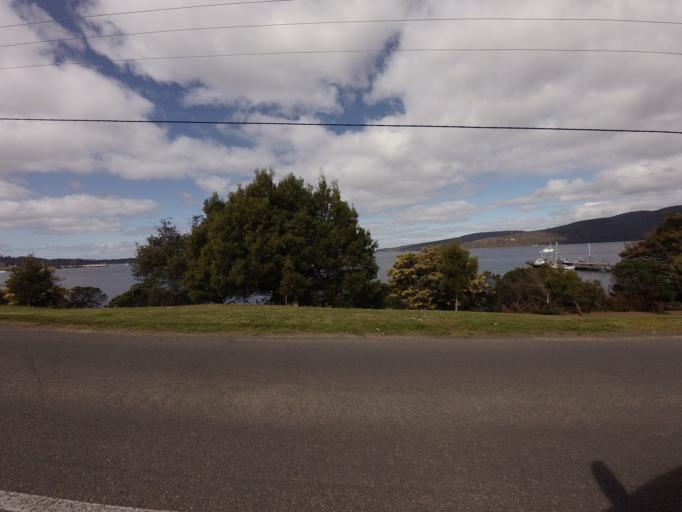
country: AU
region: Tasmania
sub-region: Huon Valley
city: Geeveston
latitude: -43.3193
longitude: 147.0086
